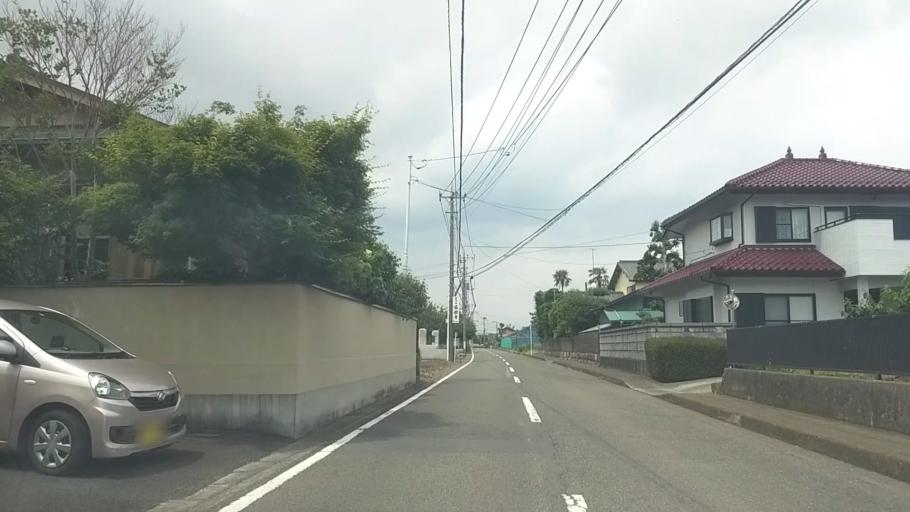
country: JP
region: Kanagawa
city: Chigasaki
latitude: 35.3862
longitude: 139.4133
